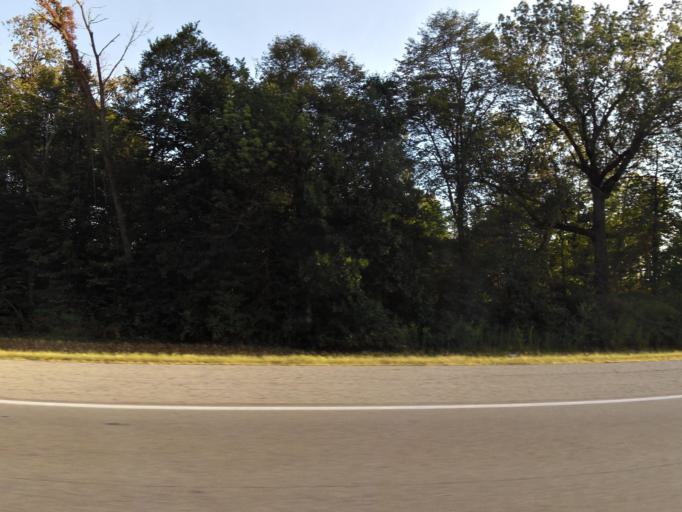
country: US
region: Indiana
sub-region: Boone County
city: Zionsville
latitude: 39.9315
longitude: -86.3116
